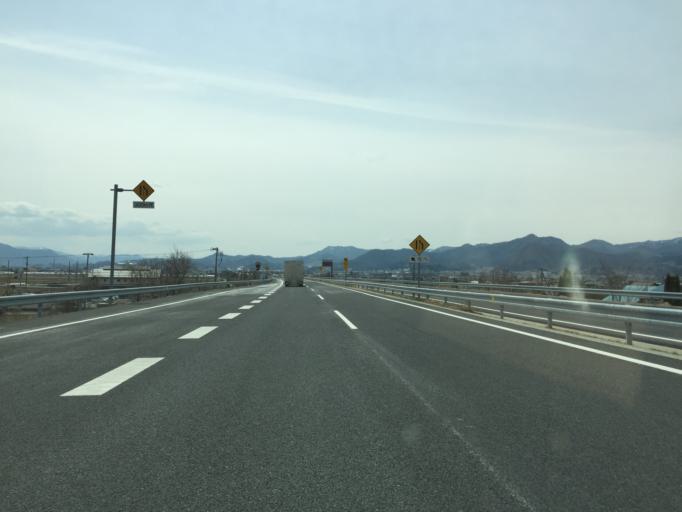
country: JP
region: Yamagata
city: Yamagata-shi
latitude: 38.2688
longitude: 140.2923
